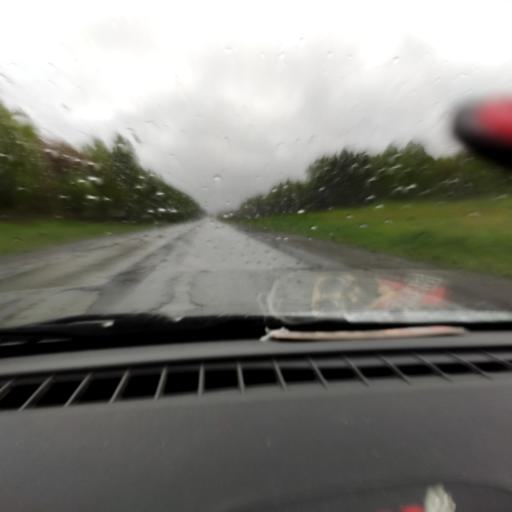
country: RU
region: Perm
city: Kukushtan
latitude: 57.6054
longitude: 56.5141
